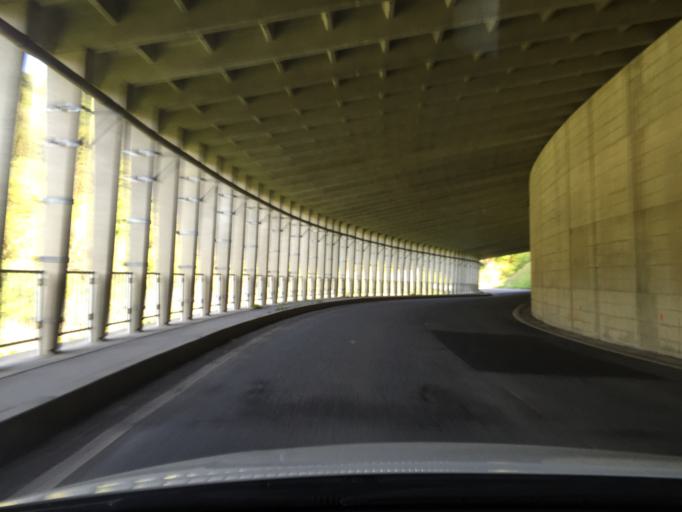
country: JP
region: Fukushima
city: Kitakata
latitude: 37.6705
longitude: 139.7337
